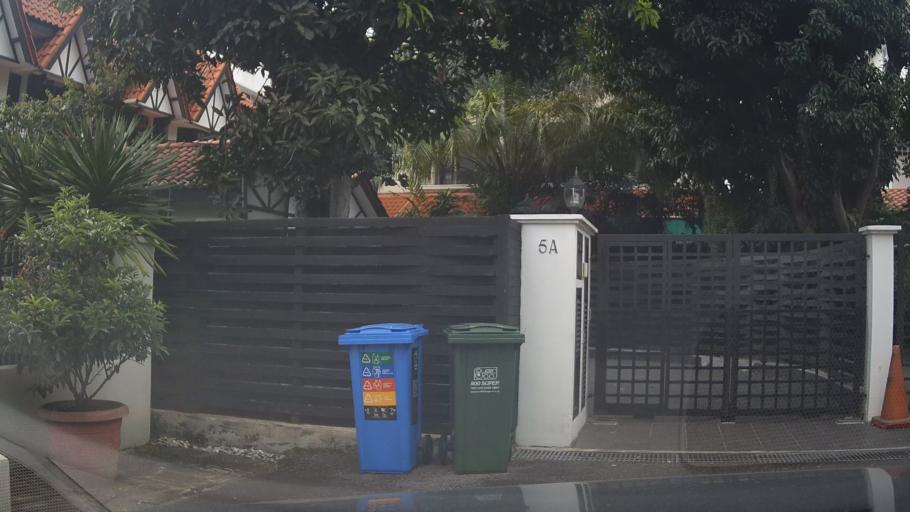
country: SG
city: Singapore
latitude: 1.3127
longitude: 103.9302
